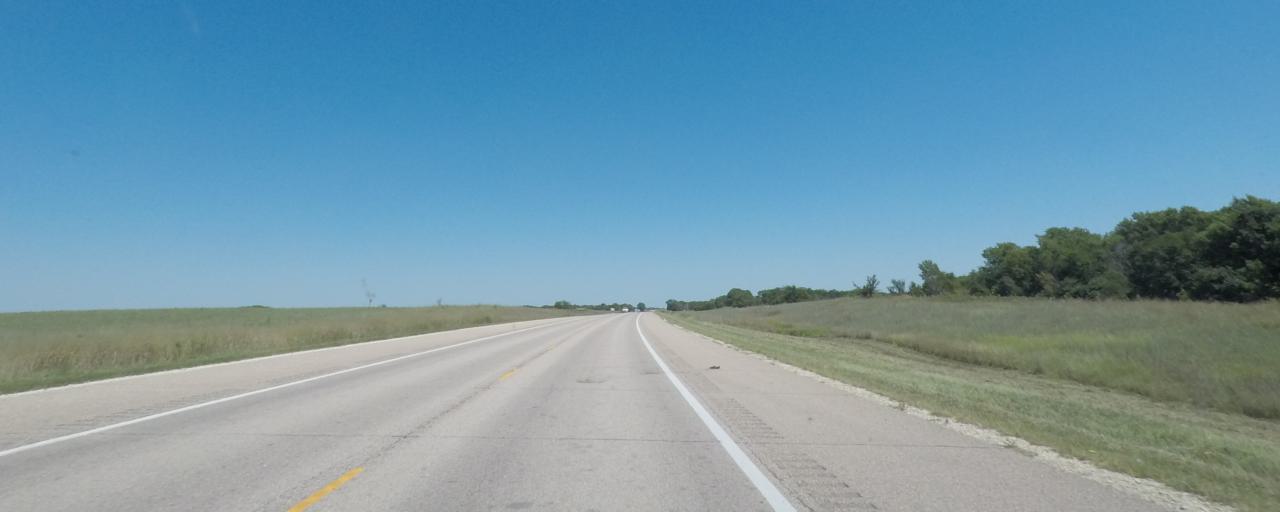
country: US
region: Kansas
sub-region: Marion County
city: Peabody
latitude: 38.1951
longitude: -97.0328
